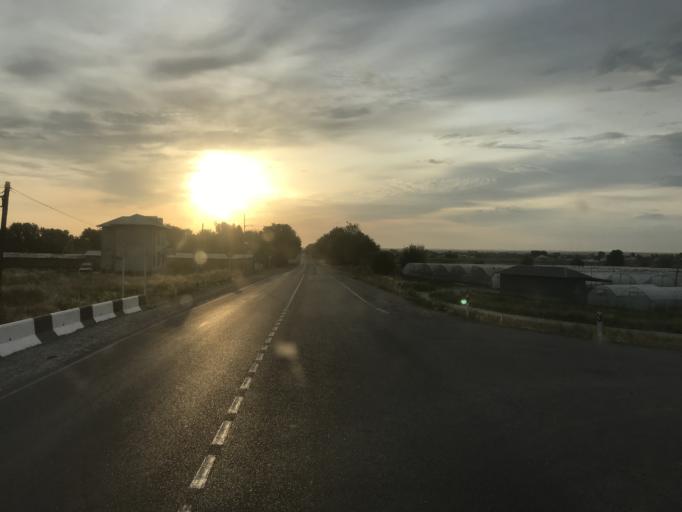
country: UZ
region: Toshkent
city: Yangiyul
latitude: 41.3291
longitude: 68.8994
